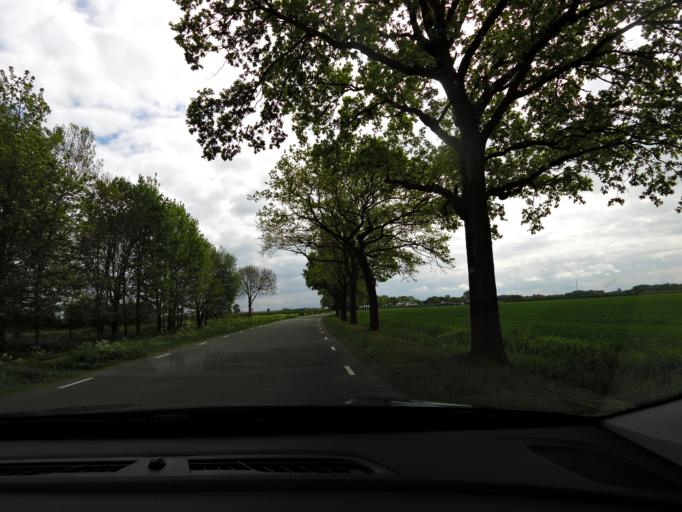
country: NL
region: Gelderland
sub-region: Gemeente Tiel
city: Tiel
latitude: 51.9327
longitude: 5.4510
